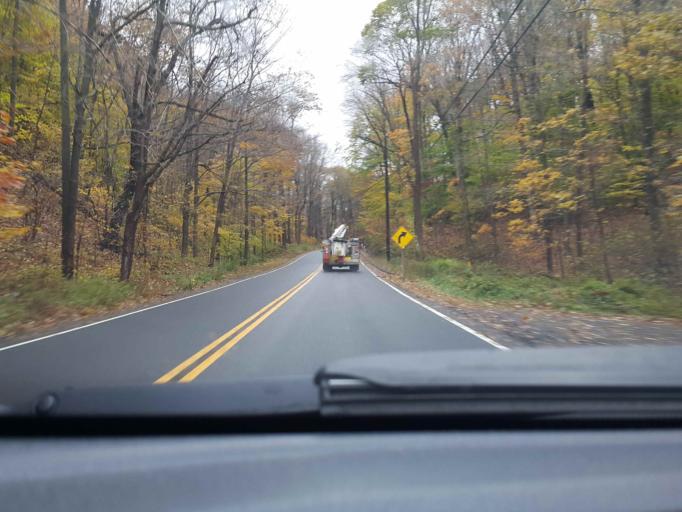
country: US
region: Connecticut
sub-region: Middlesex County
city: Durham
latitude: 41.4081
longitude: -72.6962
